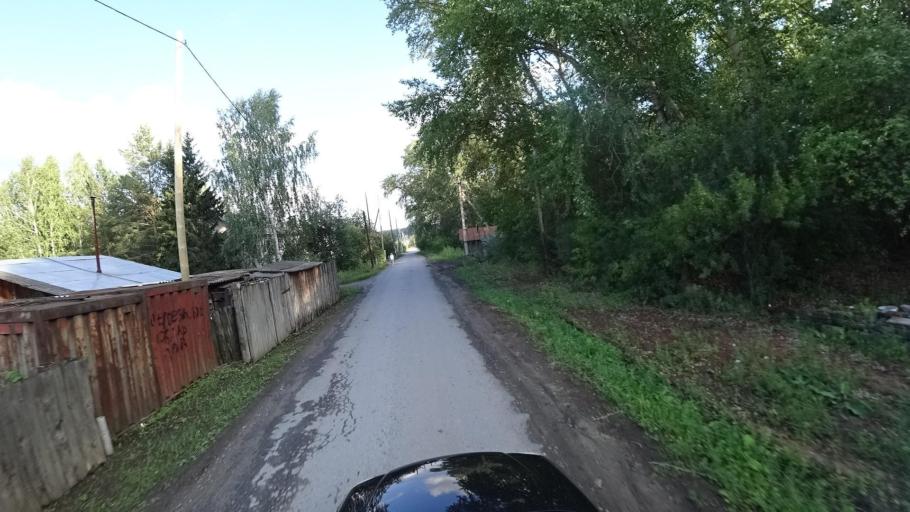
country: RU
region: Sverdlovsk
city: Obukhovskoye
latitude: 56.8487
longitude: 62.6535
